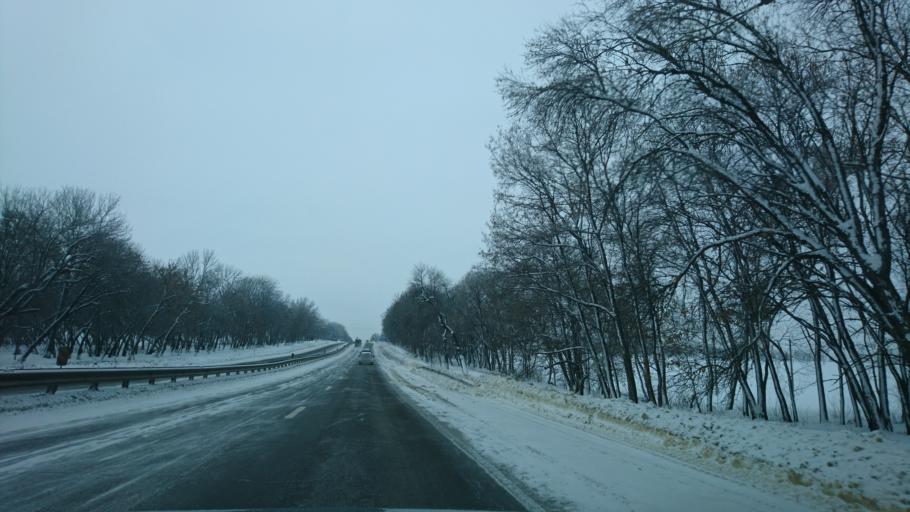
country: RU
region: Belgorod
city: Mayskiy
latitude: 50.4403
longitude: 36.3934
